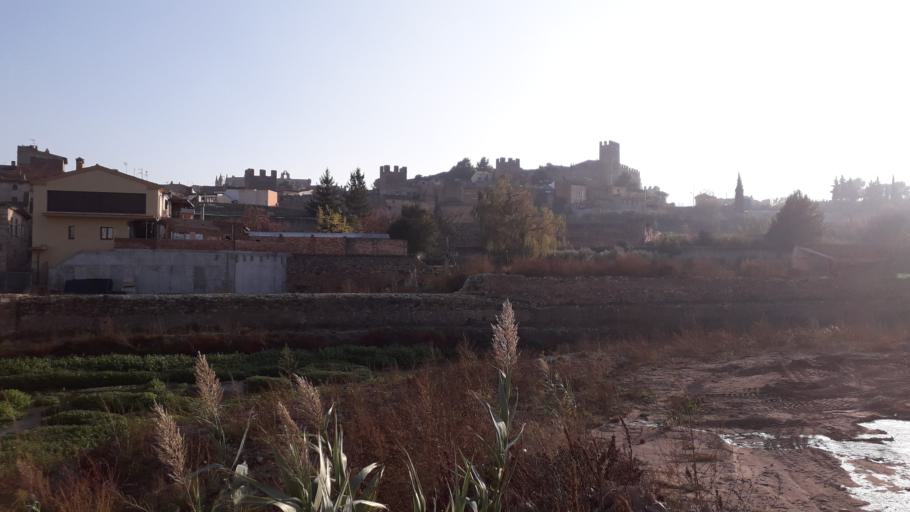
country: ES
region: Catalonia
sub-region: Provincia de Tarragona
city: Montblanc
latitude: 41.3806
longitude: 1.1610
